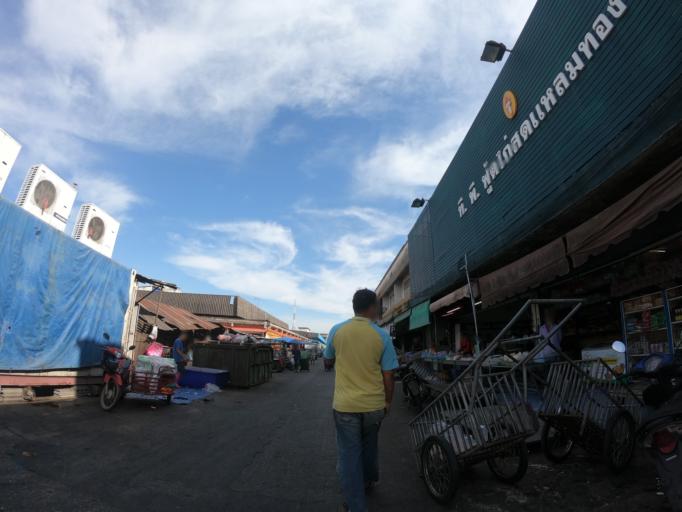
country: TH
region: Khon Kaen
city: Khon Kaen
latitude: 16.4370
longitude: 102.8323
